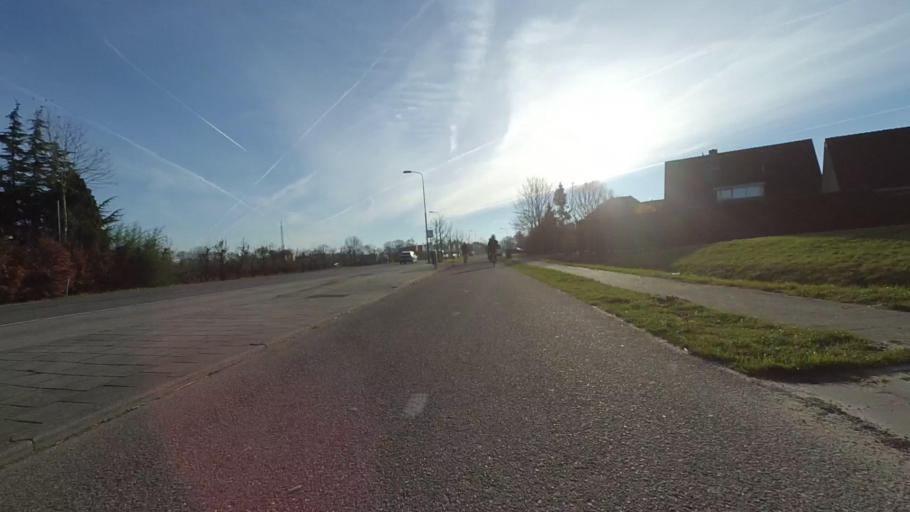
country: NL
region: Utrecht
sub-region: Gemeente Wijk bij Duurstede
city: Wijk bij Duurstede
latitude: 51.9845
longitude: 5.3372
